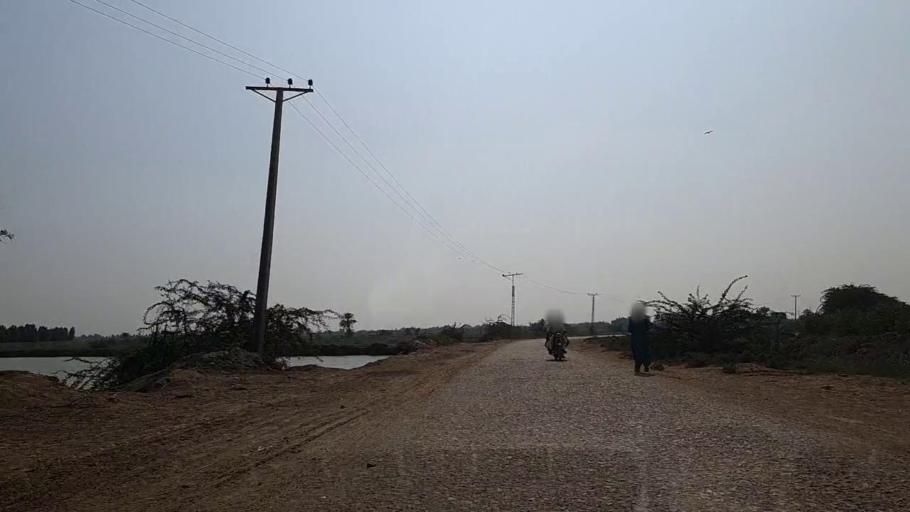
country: PK
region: Sindh
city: Thatta
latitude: 24.7375
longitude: 67.7703
